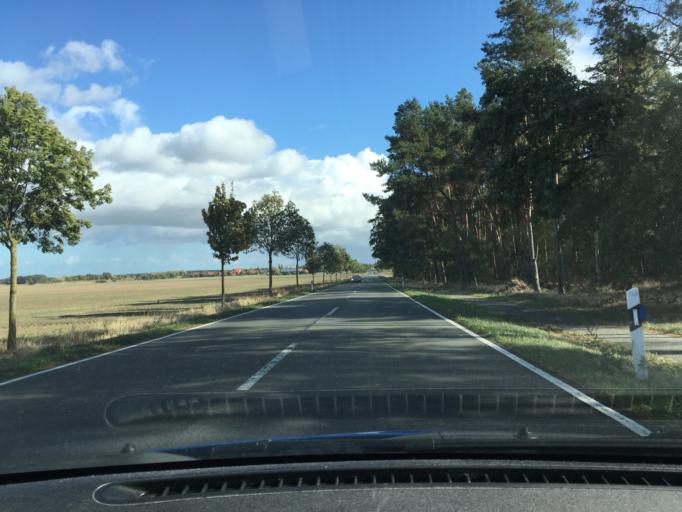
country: DE
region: Saxony-Anhalt
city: Pretzier
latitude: 52.8369
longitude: 11.2392
